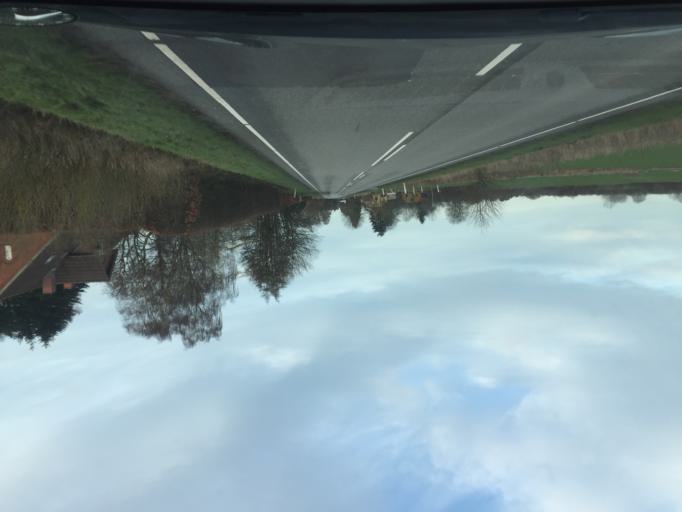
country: DK
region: South Denmark
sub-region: Faaborg-Midtfyn Kommune
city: Ringe
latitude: 55.2244
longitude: 10.4525
